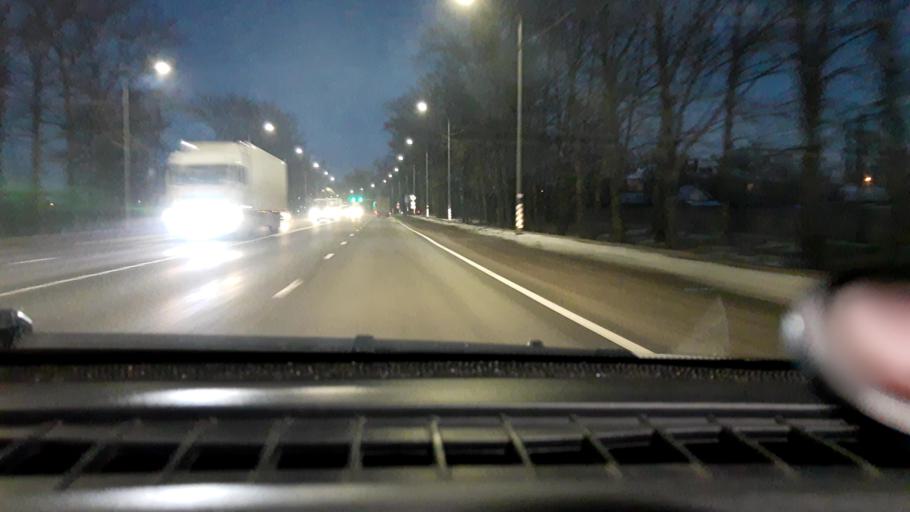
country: RU
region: Nizjnij Novgorod
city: Lyskovo
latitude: 56.0141
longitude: 45.0221
